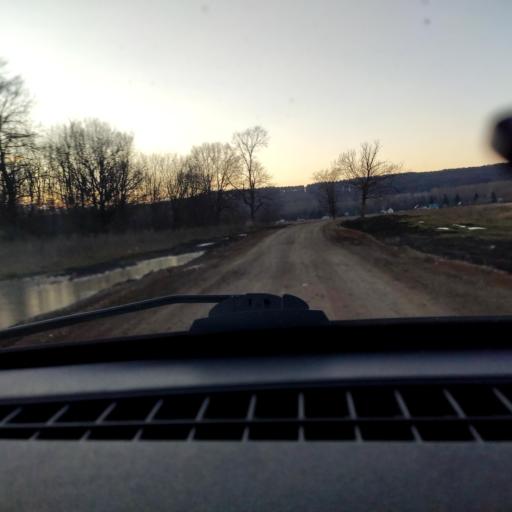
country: RU
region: Bashkortostan
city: Ufa
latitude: 54.7375
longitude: 56.0559
